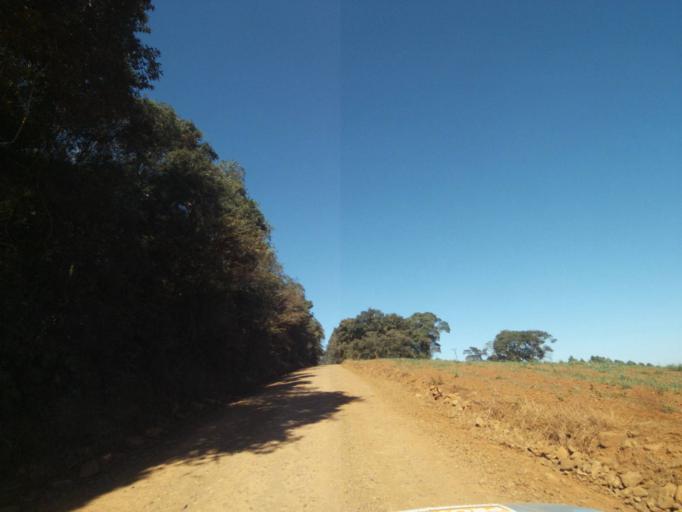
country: BR
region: Parana
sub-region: Tibagi
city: Tibagi
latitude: -24.5899
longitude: -50.6062
